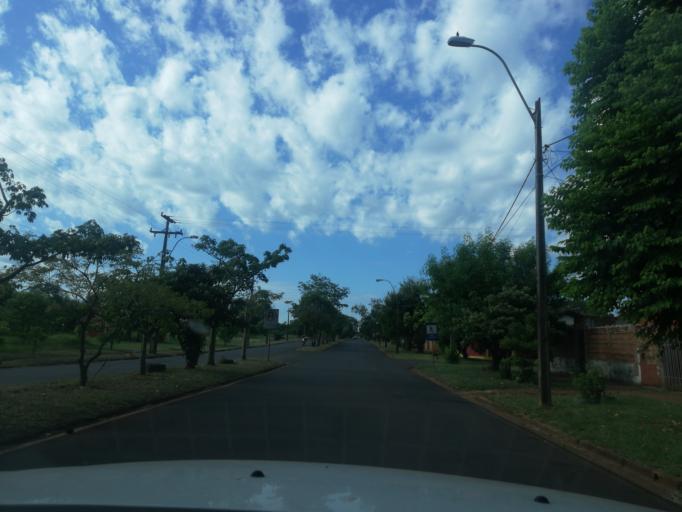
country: PY
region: Itapua
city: Encarnacion
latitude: -27.3488
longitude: -55.8490
